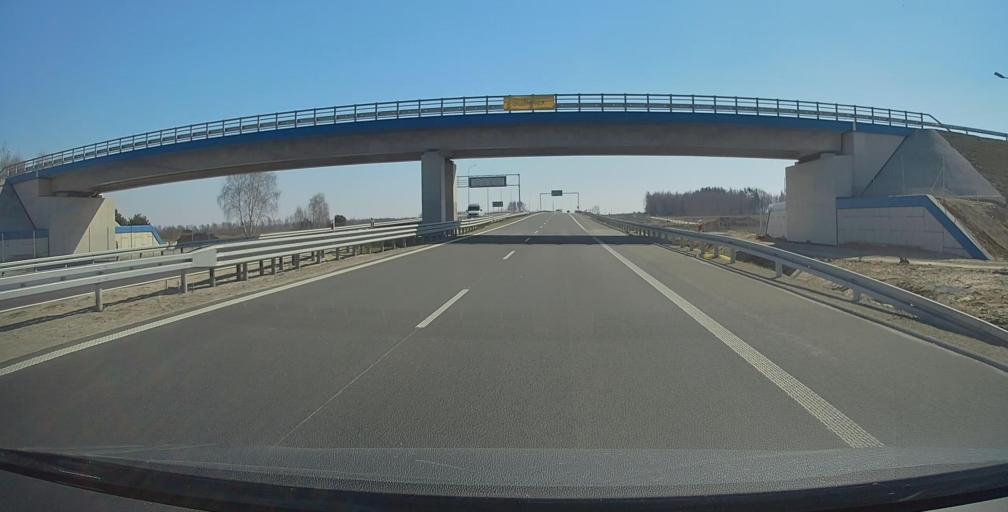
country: PL
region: Subcarpathian Voivodeship
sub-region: Powiat rzeszowski
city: Gorno
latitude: 50.2577
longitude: 22.1292
